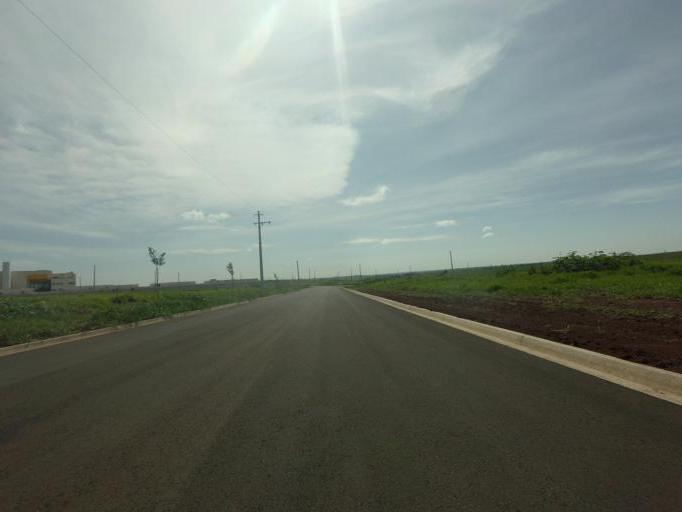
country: BR
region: Sao Paulo
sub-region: Piracicaba
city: Piracicaba
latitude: -22.7642
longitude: -47.5852
